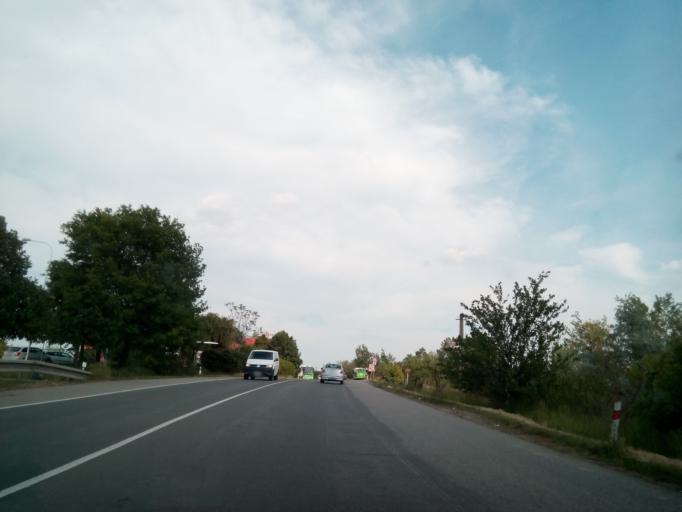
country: CZ
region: South Moravian
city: Tvarozna
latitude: 49.1840
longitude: 16.7587
